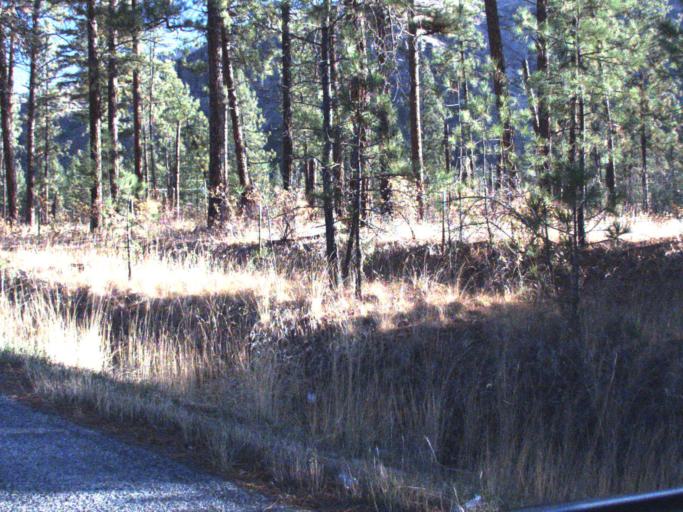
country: US
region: Washington
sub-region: Okanogan County
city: Coulee Dam
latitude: 48.0897
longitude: -118.6922
